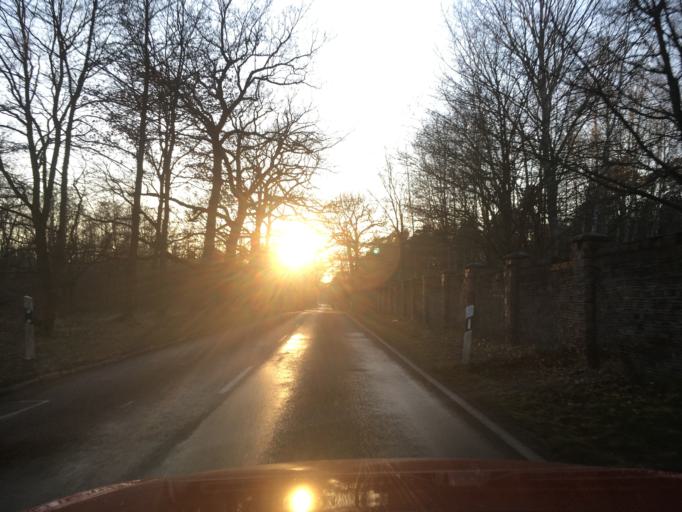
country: DE
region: Saxony-Anhalt
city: Rosslau
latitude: 51.9003
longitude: 12.2743
